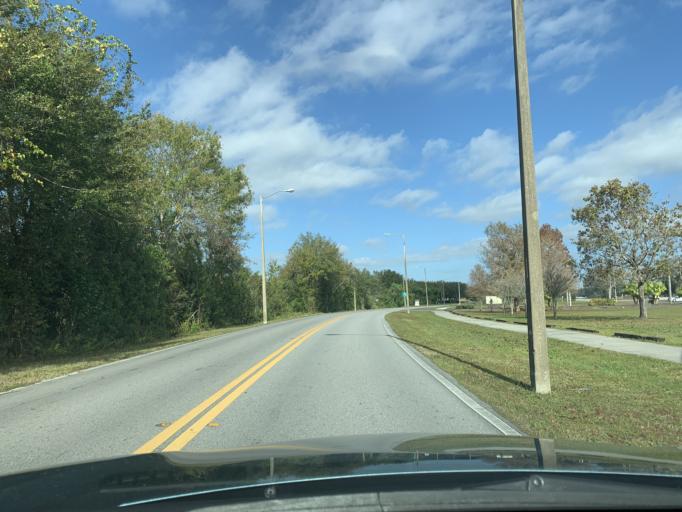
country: US
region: Florida
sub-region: Pasco County
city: Trinity
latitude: 28.1935
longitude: -82.6799
